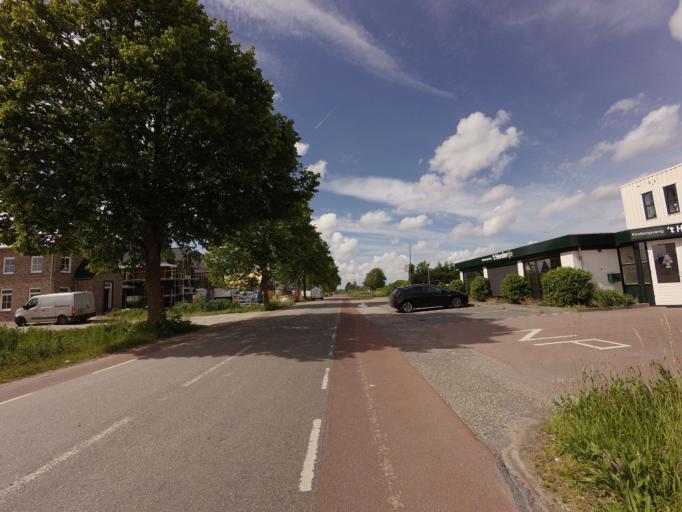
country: NL
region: North Holland
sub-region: Gemeente Hoorn
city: Hoorn
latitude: 52.6714
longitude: 5.0987
